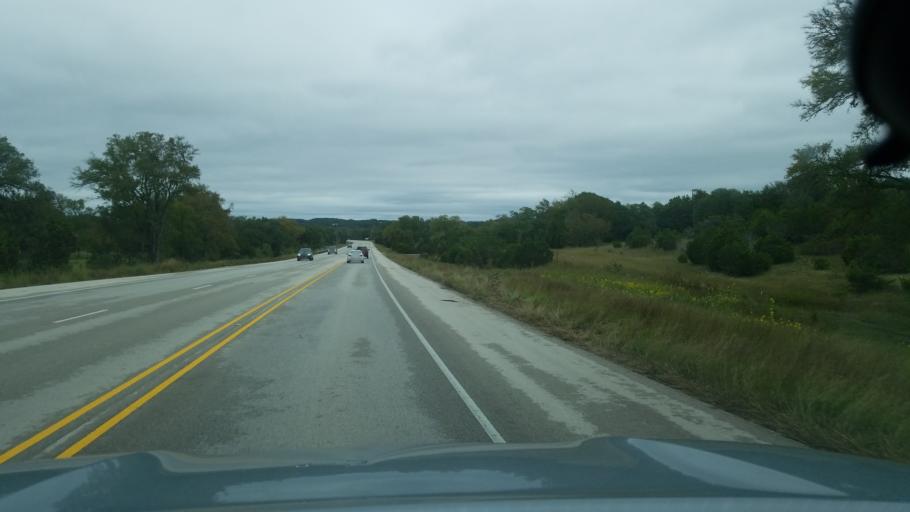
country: US
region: Texas
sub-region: Blanco County
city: Blanco
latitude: 29.9912
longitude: -98.4076
